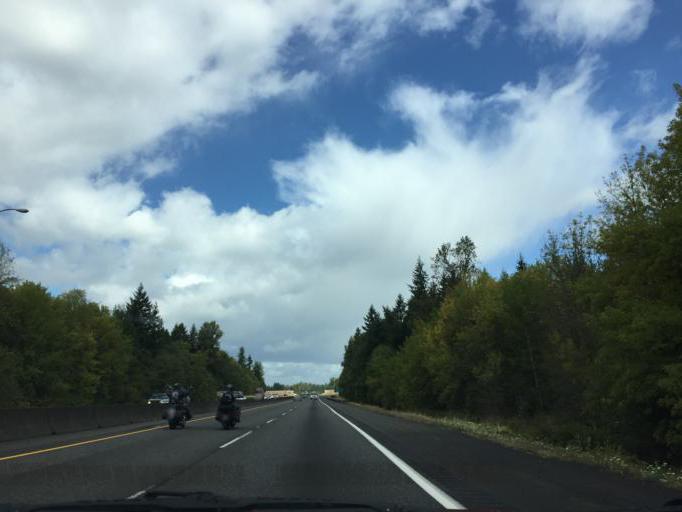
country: US
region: Washington
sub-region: Cowlitz County
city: Castle Rock
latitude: 46.3821
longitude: -122.9040
